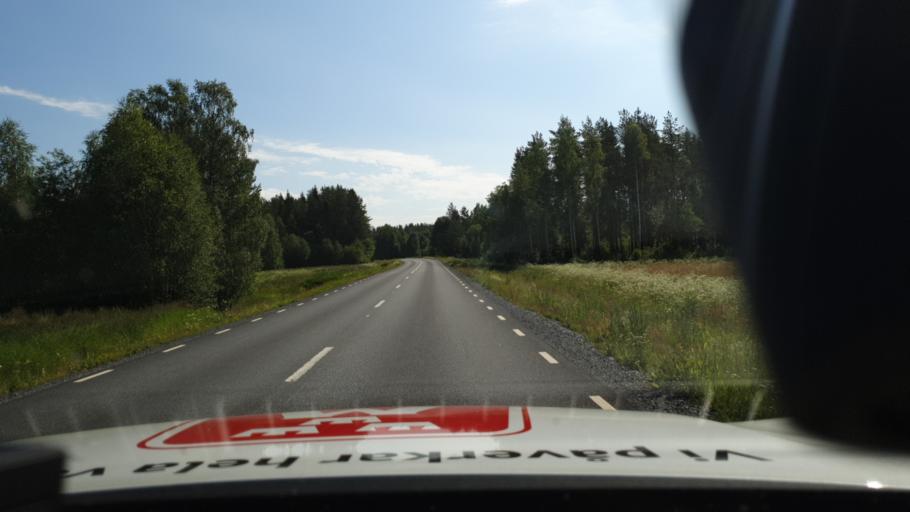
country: SE
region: Norrbotten
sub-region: Bodens Kommun
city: Boden
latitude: 65.8439
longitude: 21.7564
